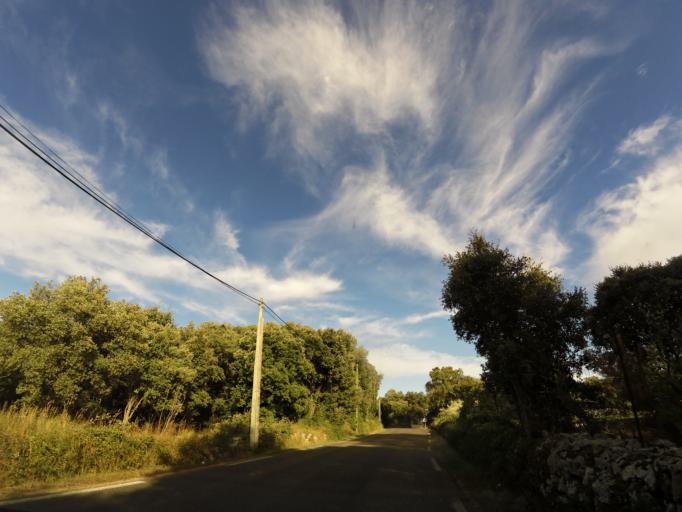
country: FR
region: Languedoc-Roussillon
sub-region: Departement de l'Herault
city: Boisseron
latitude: 43.7777
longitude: 4.0637
